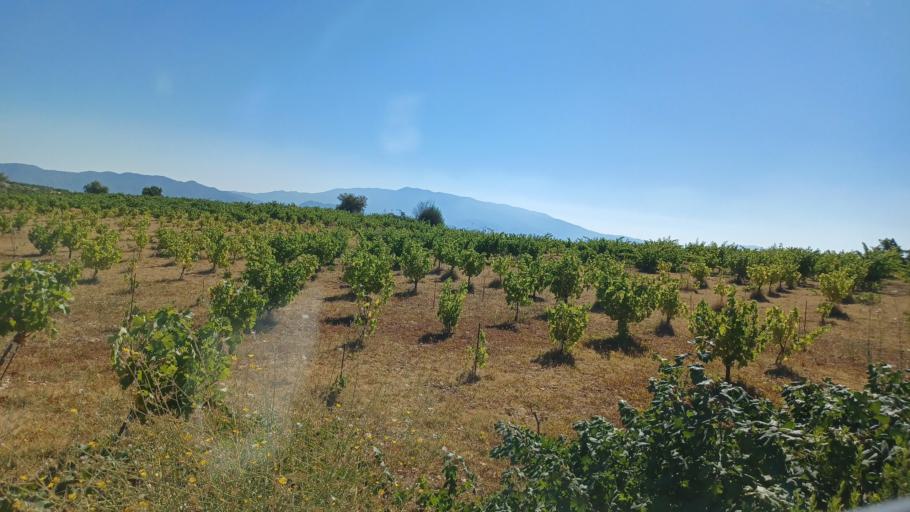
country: CY
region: Limassol
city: Pachna
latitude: 34.9045
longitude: 32.6407
